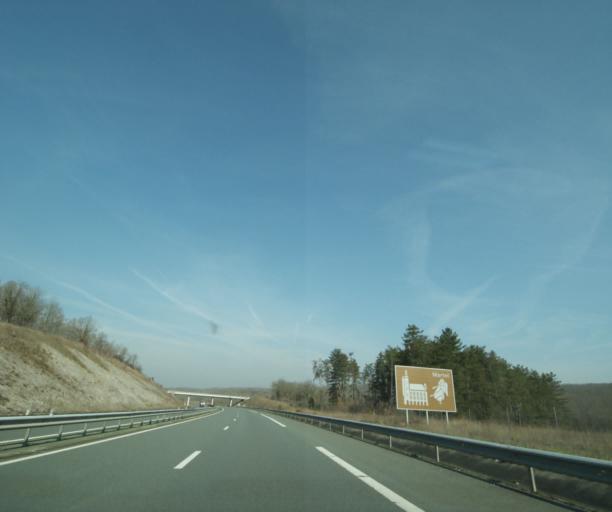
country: FR
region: Midi-Pyrenees
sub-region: Departement du Lot
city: Le Vigan
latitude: 44.7850
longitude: 1.5298
